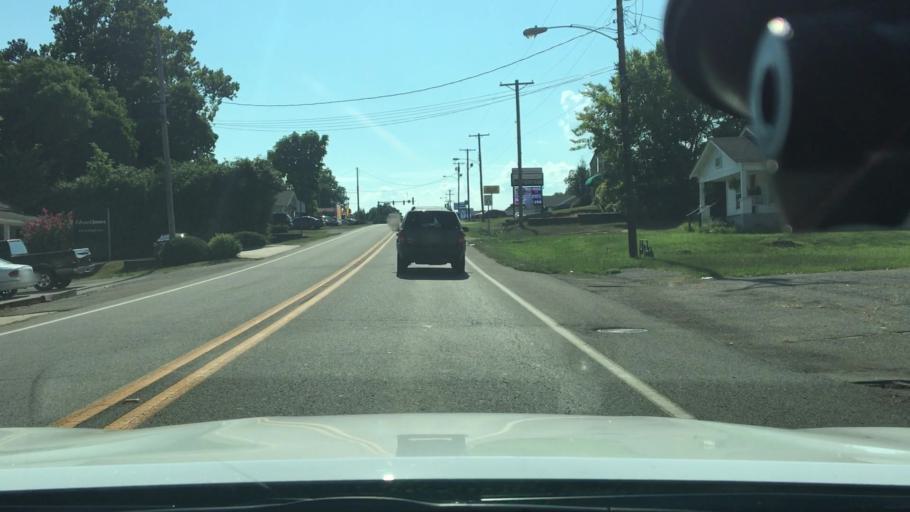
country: US
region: Arkansas
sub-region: Johnson County
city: Clarksville
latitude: 35.4715
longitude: -93.4763
